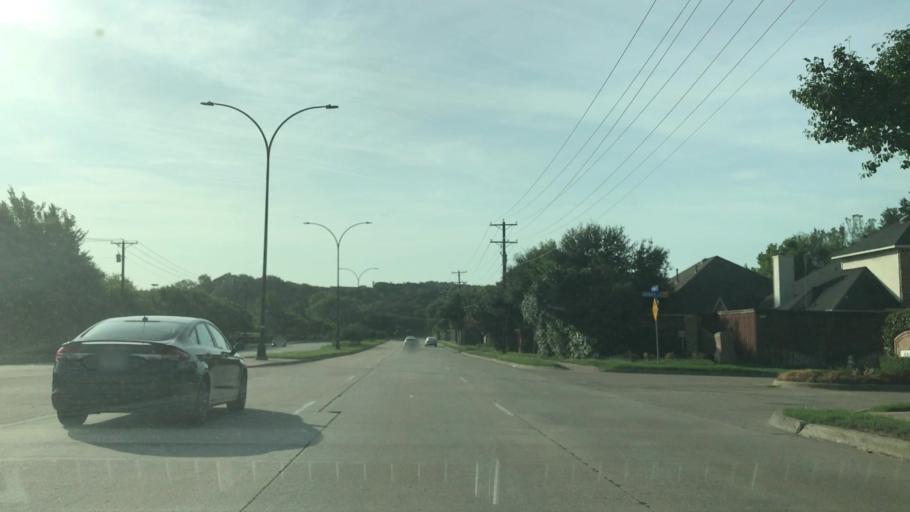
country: US
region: Texas
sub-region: Tarrant County
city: Arlington
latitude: 32.7826
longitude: -97.0900
